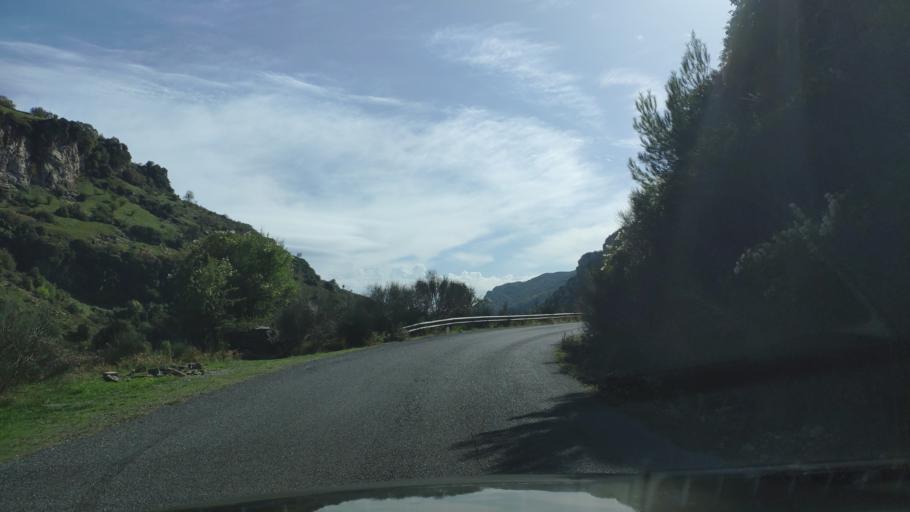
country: GR
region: Peloponnese
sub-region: Nomos Arkadias
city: Dimitsana
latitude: 37.5998
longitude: 22.0346
